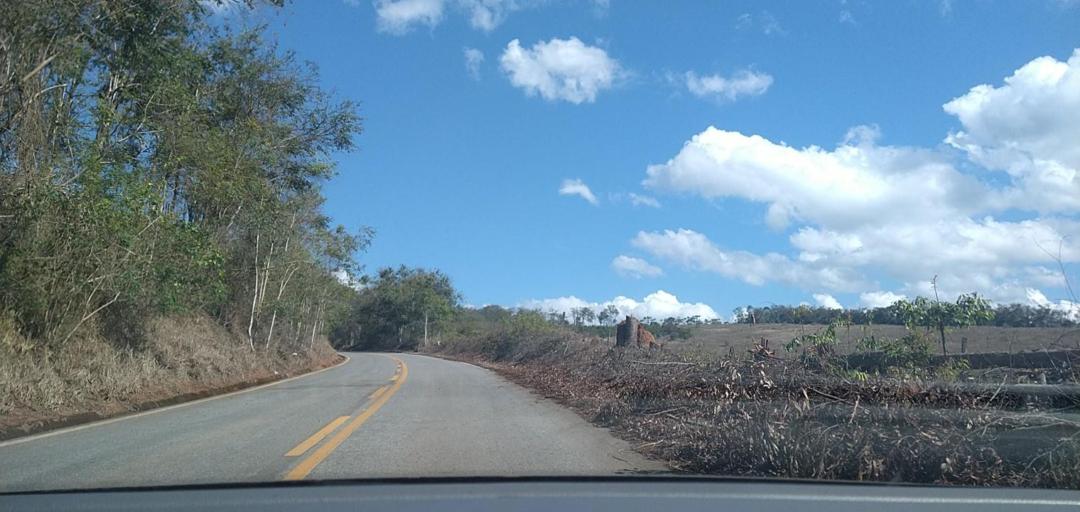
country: BR
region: Minas Gerais
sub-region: Alvinopolis
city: Alvinopolis
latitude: -20.0341
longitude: -43.0457
